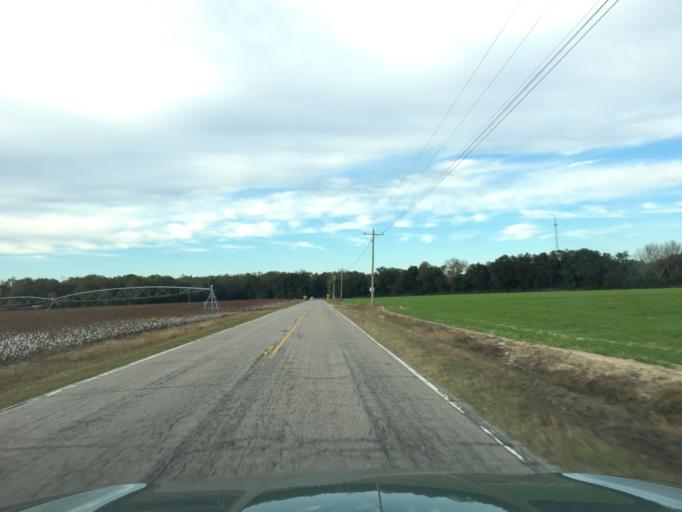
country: US
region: South Carolina
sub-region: Lexington County
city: Leesville
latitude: 33.7531
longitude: -81.3663
